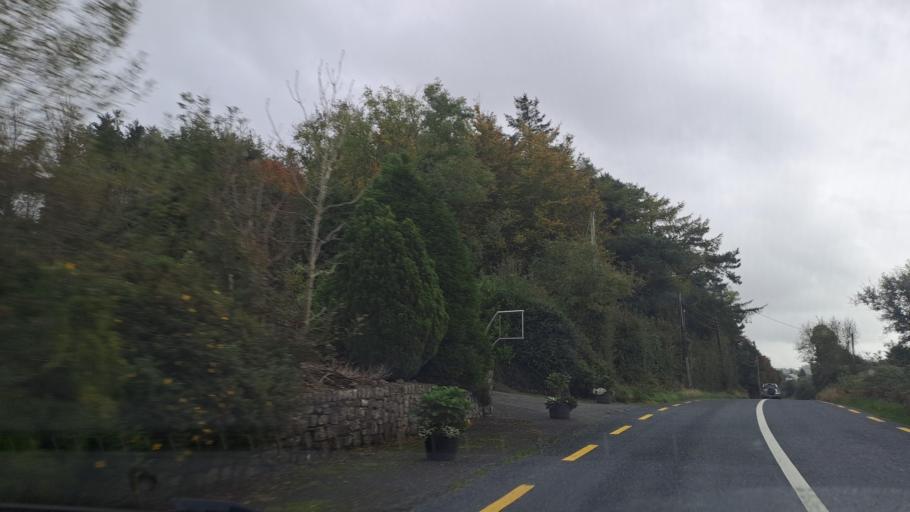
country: IE
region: Ulster
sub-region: An Cabhan
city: Bailieborough
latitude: 53.9304
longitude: -7.0083
